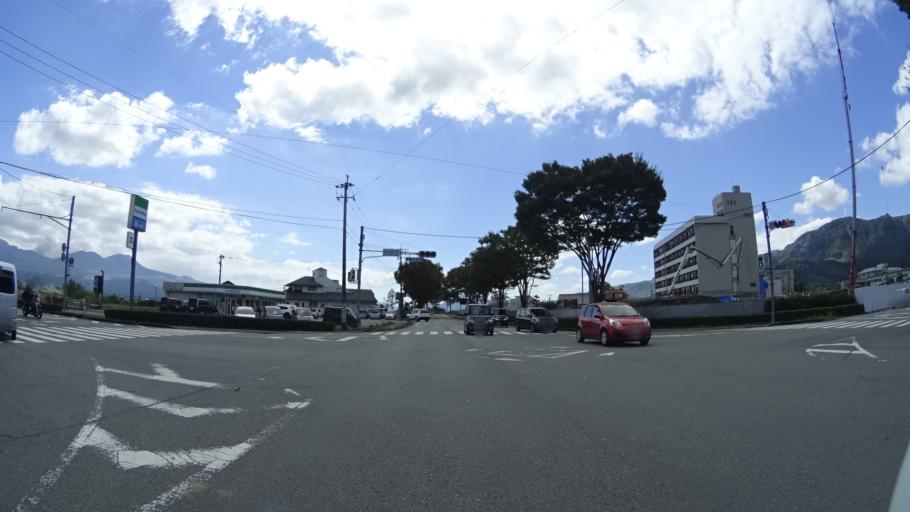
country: JP
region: Kumamoto
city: Aso
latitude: 32.9706
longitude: 131.0479
